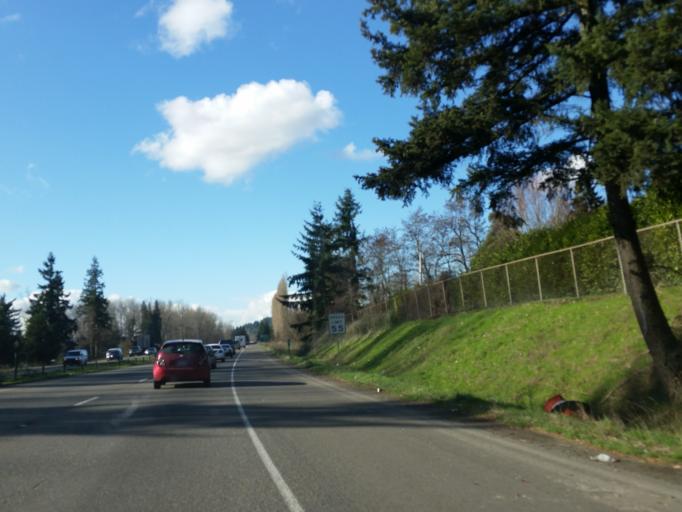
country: US
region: Washington
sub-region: Pierce County
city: Sumner
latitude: 47.1922
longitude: -122.2366
